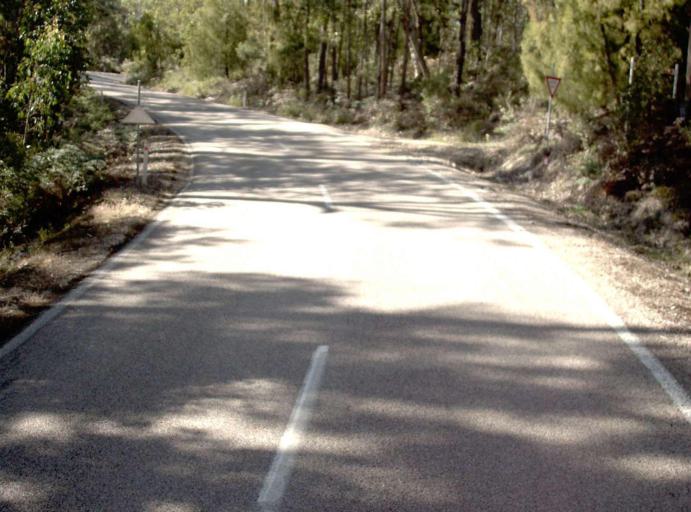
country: AU
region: Victoria
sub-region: East Gippsland
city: Lakes Entrance
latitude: -37.5686
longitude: 148.5489
